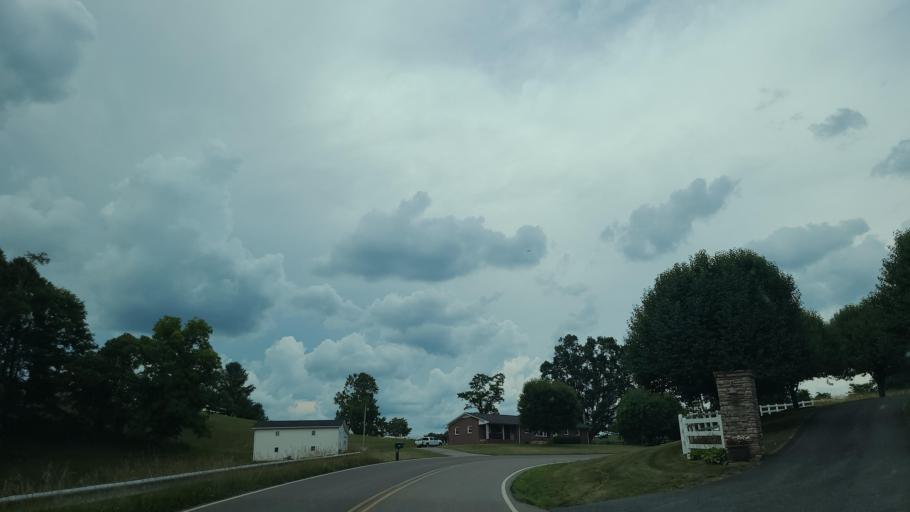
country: US
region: North Carolina
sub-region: Ashe County
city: Jefferson
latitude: 36.3993
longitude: -81.4052
